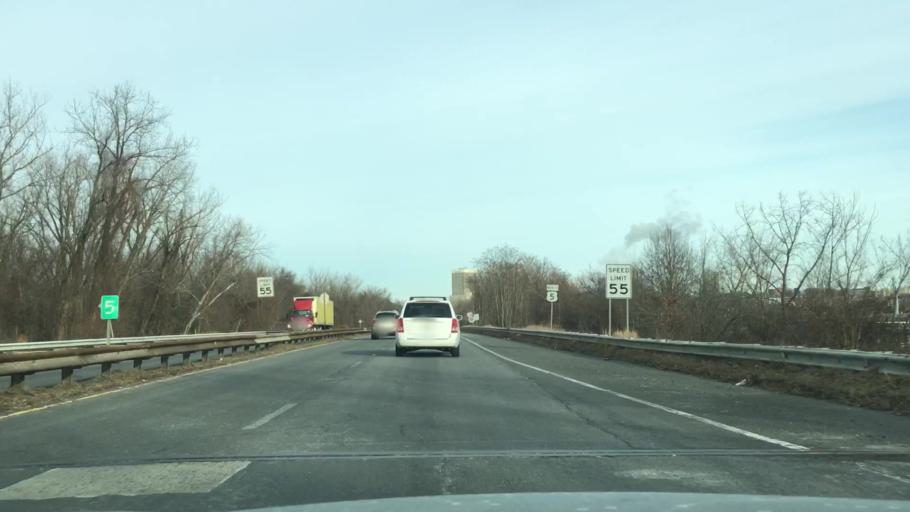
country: US
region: Massachusetts
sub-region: Hampden County
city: Springfield
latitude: 42.0846
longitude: -72.5916
